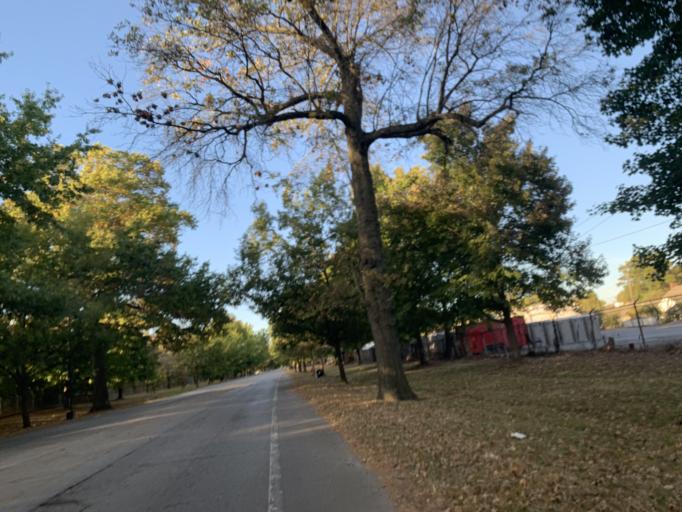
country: US
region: Kentucky
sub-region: Jefferson County
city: Shively
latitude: 38.2363
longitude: -85.8309
